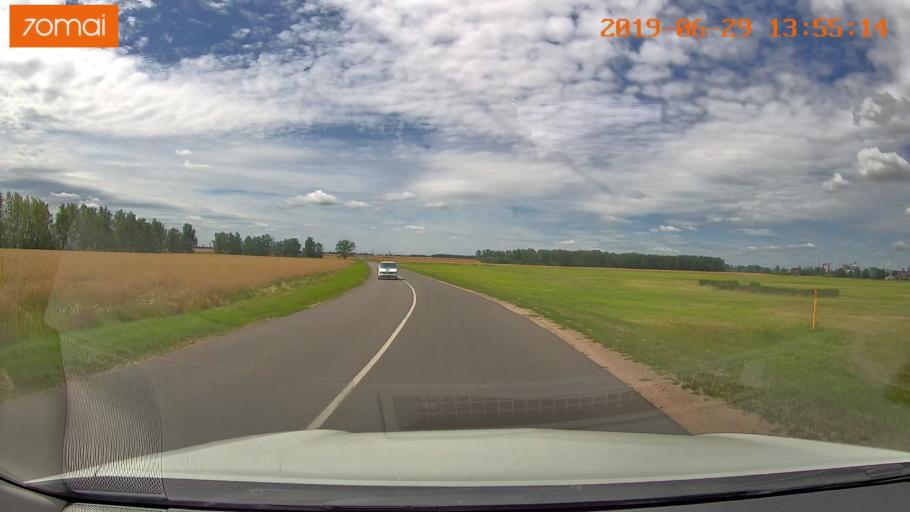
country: BY
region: Minsk
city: Slutsk
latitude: 52.9835
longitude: 27.5235
